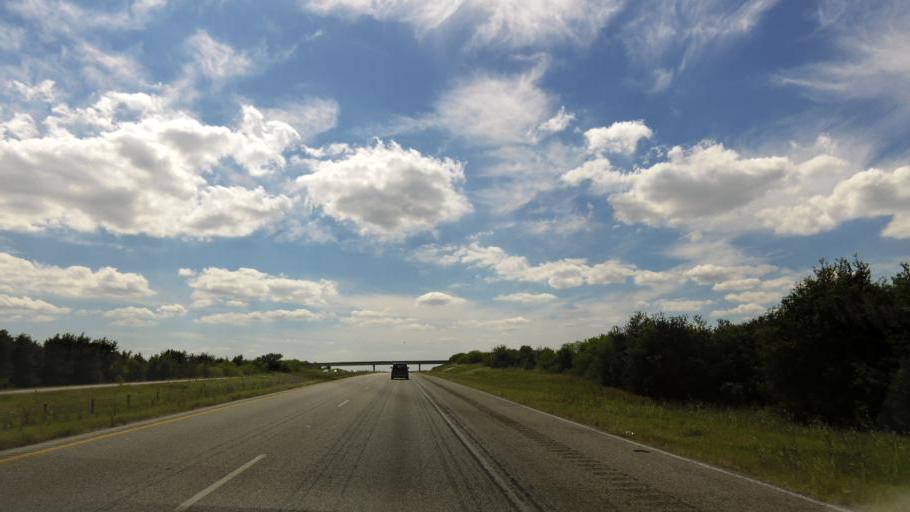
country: US
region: Texas
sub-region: Gonzales County
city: Waelder
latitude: 29.6671
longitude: -97.3304
